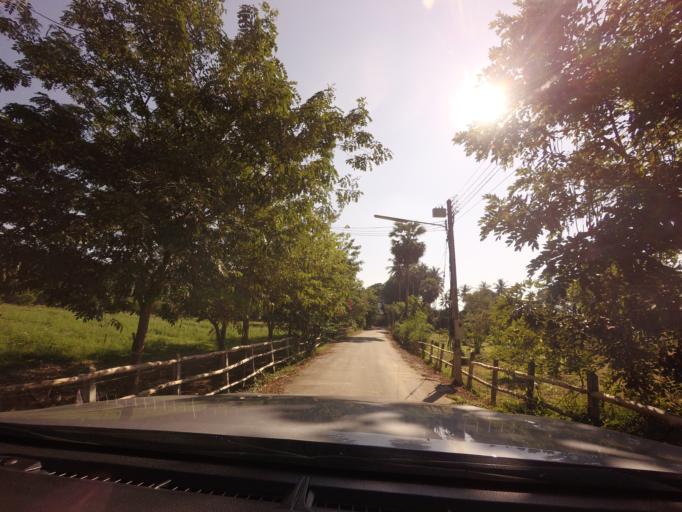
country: TH
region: Sukhothai
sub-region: Amphoe Si Satchanalai
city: Si Satchanalai
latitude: 17.6309
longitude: 99.6868
